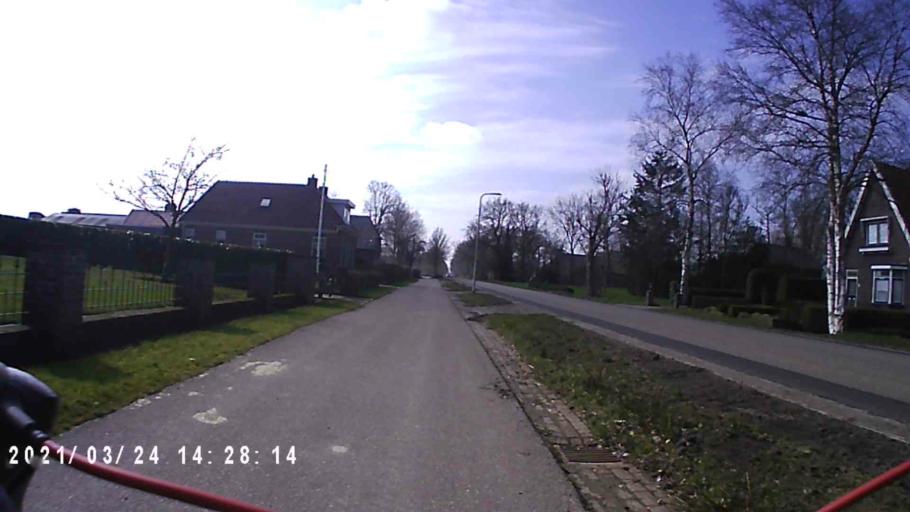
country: NL
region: Friesland
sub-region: Gemeente Heerenveen
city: Jubbega
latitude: 53.0385
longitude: 6.1674
